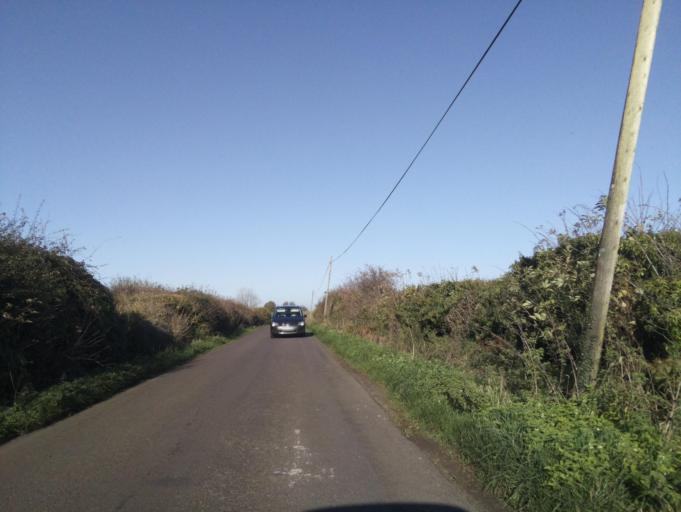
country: GB
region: England
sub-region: Dorset
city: Sherborne
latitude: 51.0023
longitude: -2.5116
